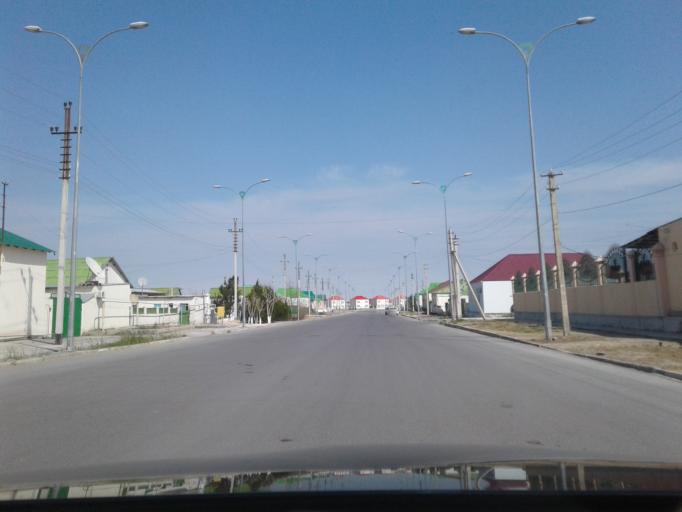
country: TM
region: Ahal
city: Ashgabat
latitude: 37.9883
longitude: 58.4021
